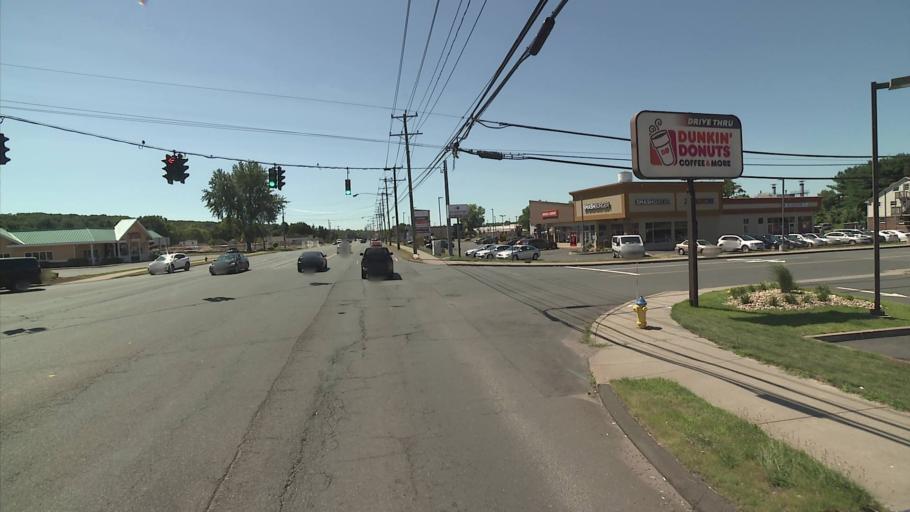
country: US
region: Connecticut
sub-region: Hartford County
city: Plainville
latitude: 41.6401
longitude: -72.8741
